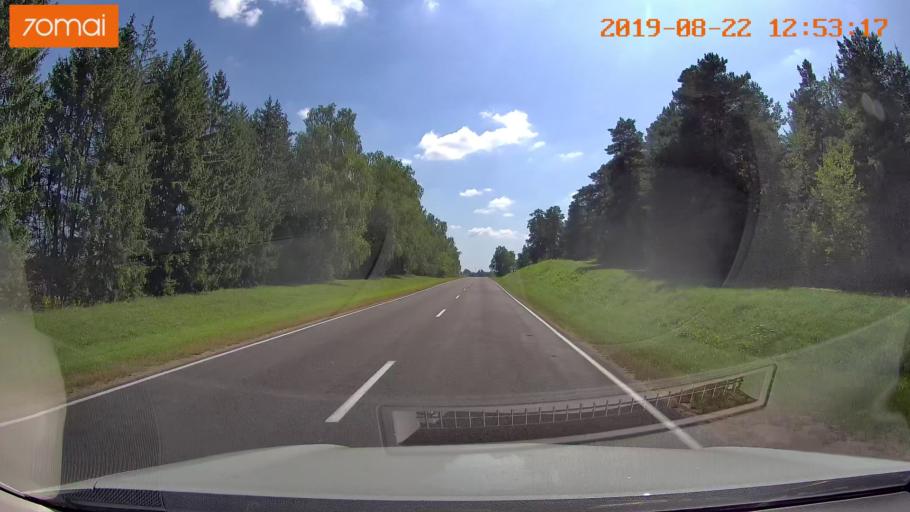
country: BY
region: Minsk
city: Prawdzinski
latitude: 53.4482
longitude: 27.6843
